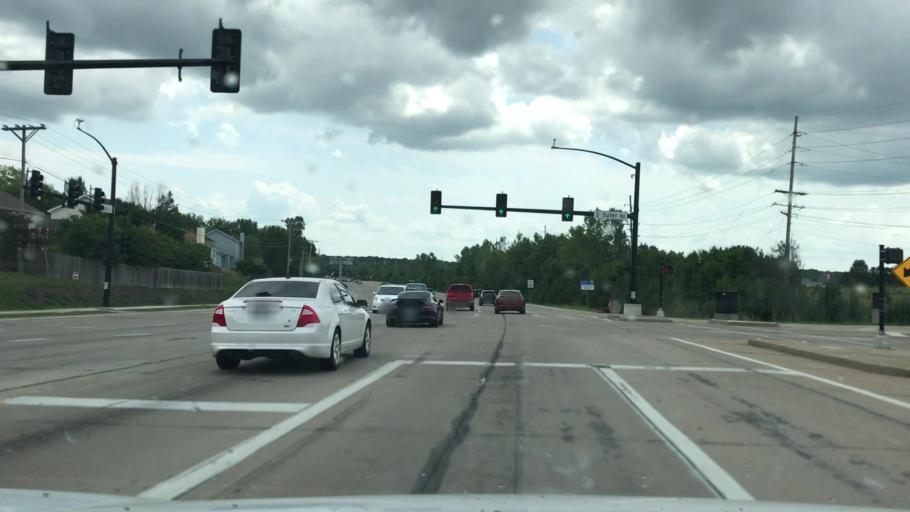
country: US
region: Missouri
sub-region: Saint Charles County
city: Dardenne Prairie
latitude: 38.7511
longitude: -90.7004
